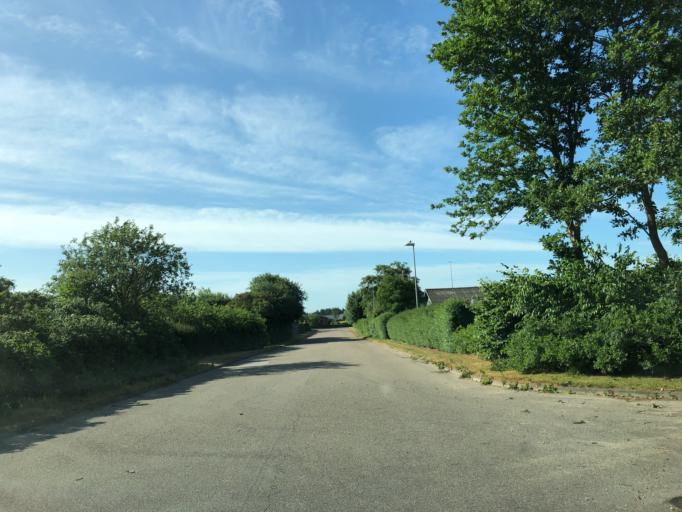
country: DK
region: Central Jutland
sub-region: Holstebro Kommune
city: Ulfborg
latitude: 56.3416
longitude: 8.3391
